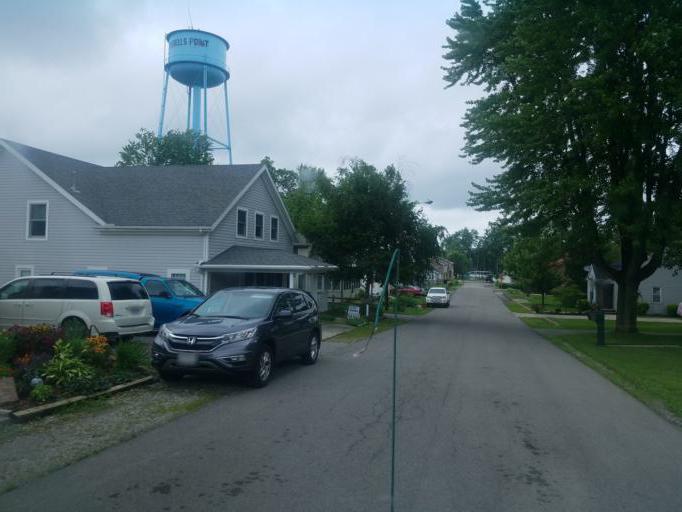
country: US
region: Ohio
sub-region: Logan County
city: Russells Point
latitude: 40.4718
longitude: -83.8918
